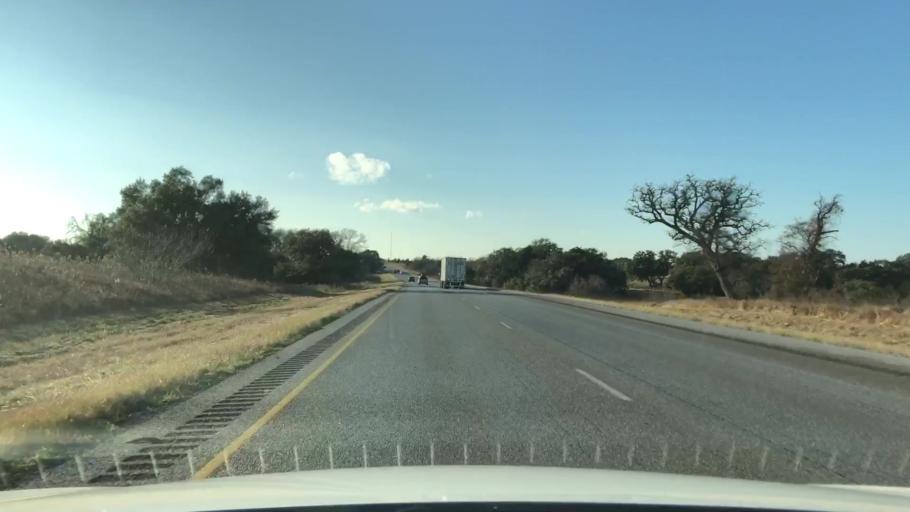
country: US
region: Texas
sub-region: Fayette County
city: Flatonia
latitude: 29.6978
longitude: -97.0440
